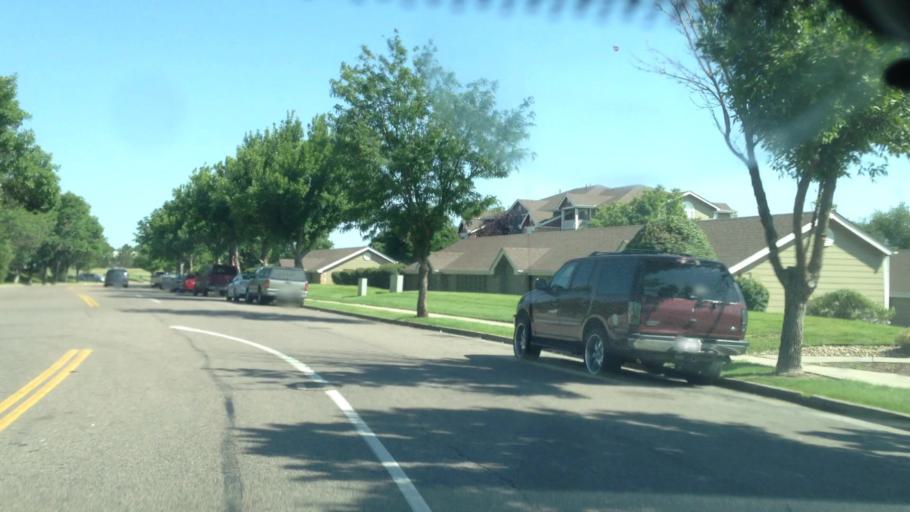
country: US
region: Colorado
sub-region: Adams County
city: Aurora
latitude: 39.7234
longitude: -104.8078
